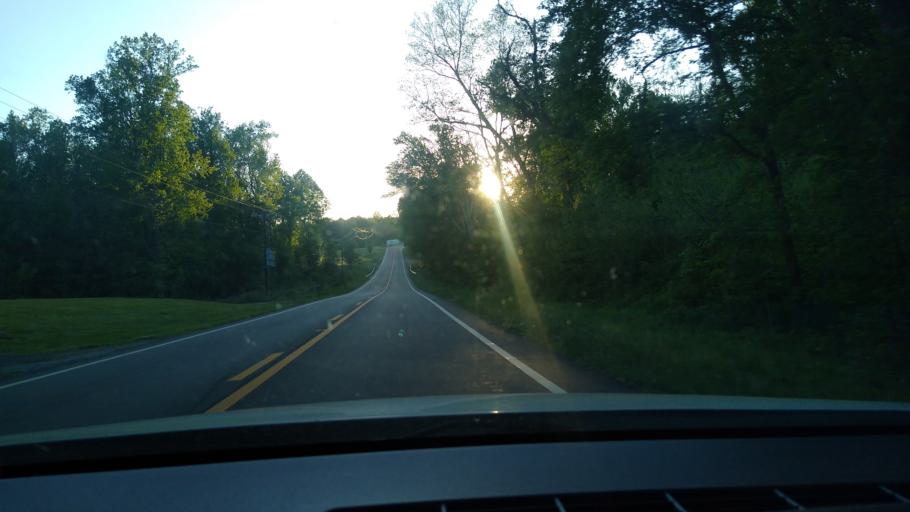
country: US
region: North Carolina
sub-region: Caswell County
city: Yanceyville
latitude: 36.3868
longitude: -79.4953
